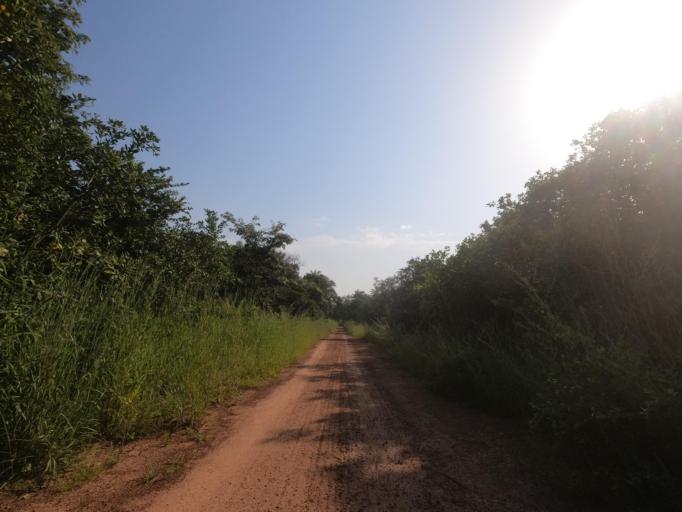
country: SN
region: Sedhiou
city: Sedhiou
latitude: 12.4392
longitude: -15.7377
